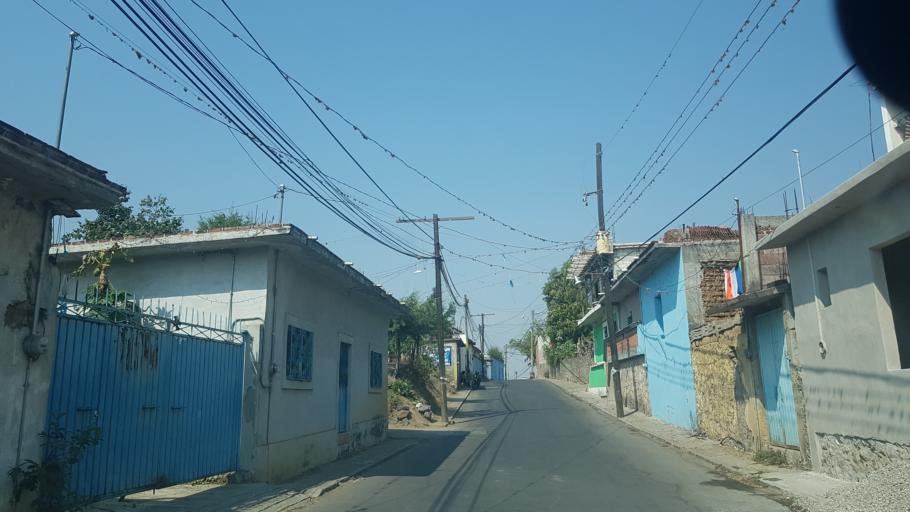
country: MX
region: Morelos
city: Tlacotepec
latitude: 18.8162
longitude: -98.7484
